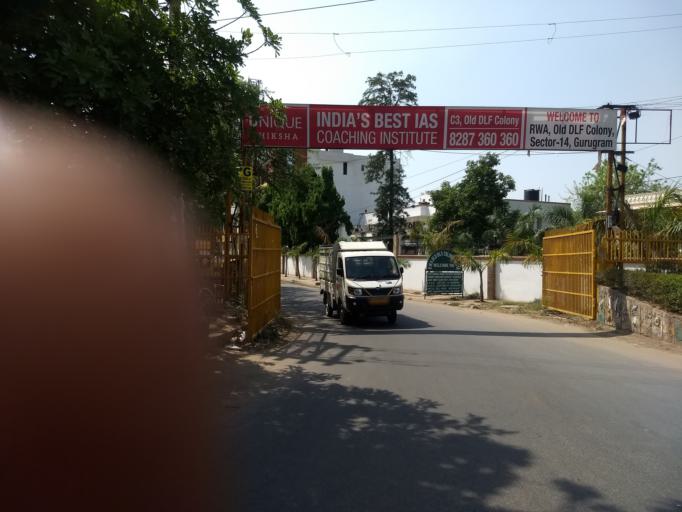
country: IN
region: Haryana
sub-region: Gurgaon
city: Gurgaon
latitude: 28.4699
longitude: 77.0464
